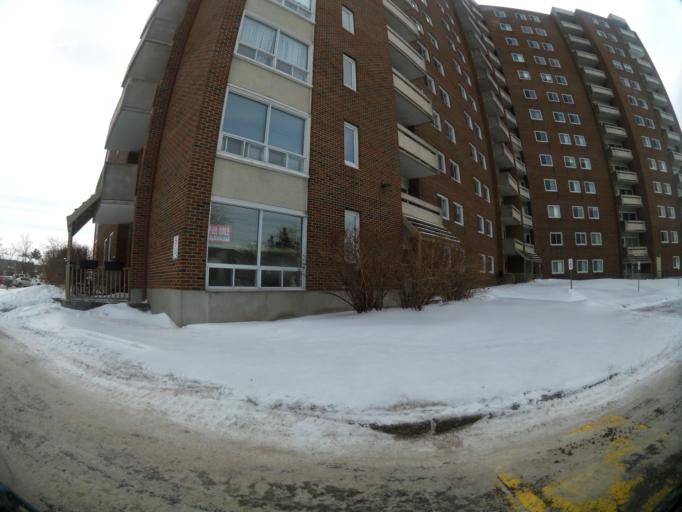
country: CA
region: Ontario
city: Ottawa
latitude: 45.4445
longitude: -75.6023
